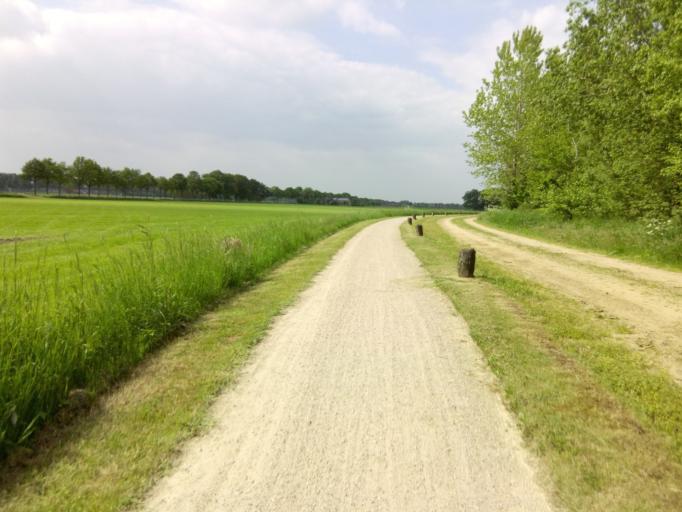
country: NL
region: Gelderland
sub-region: Berkelland
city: Borculo
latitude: 52.0528
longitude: 6.5240
